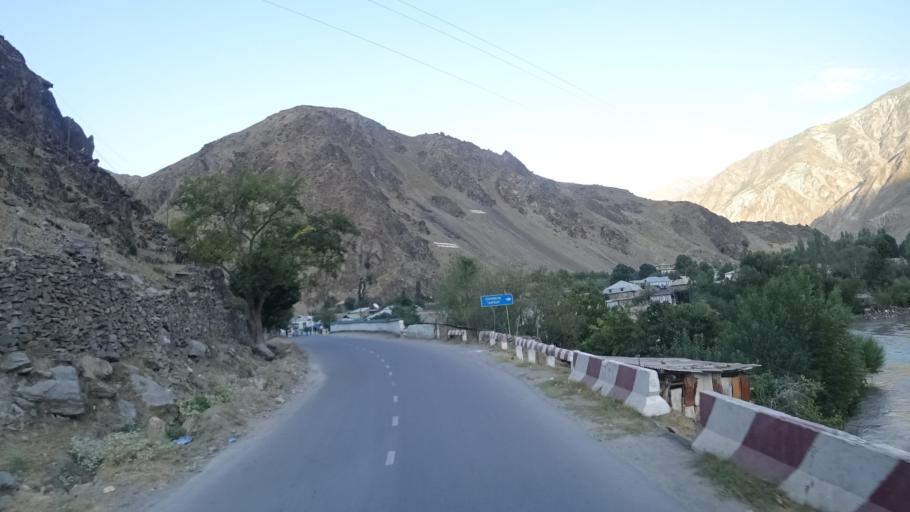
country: TJ
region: Gorno-Badakhshan
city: Qalaikhumb
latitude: 38.4566
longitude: 70.7856
